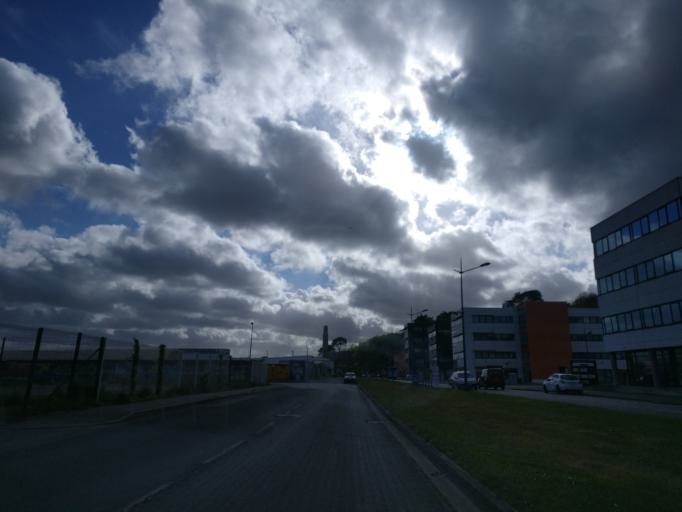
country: FR
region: Brittany
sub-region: Departement du Finistere
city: Brest
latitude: 48.3850
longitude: -4.4782
